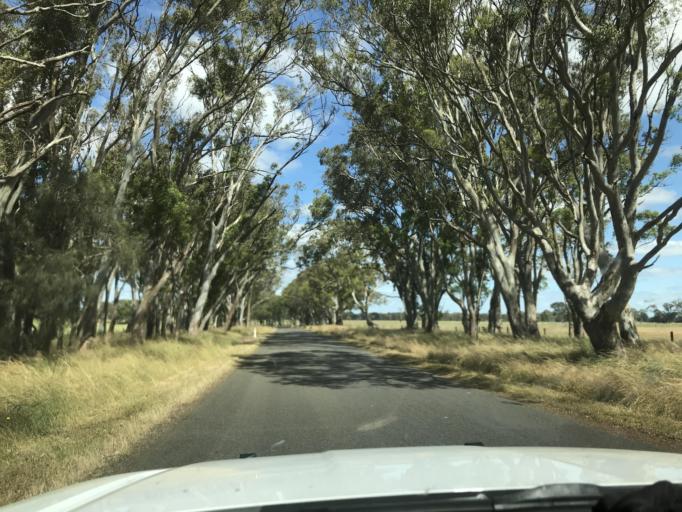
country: AU
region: South Australia
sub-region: Naracoorte and Lucindale
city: Naracoorte
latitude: -36.9902
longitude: 141.2827
